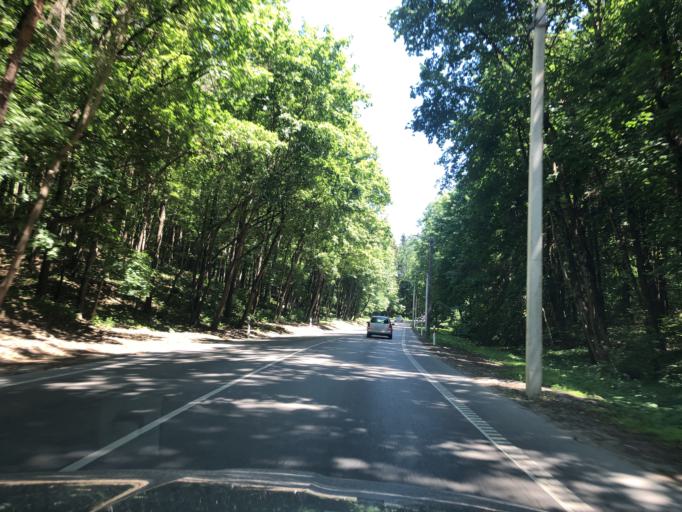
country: LT
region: Kauno apskritis
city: Dainava (Kaunas)
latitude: 54.8706
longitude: 23.9851
